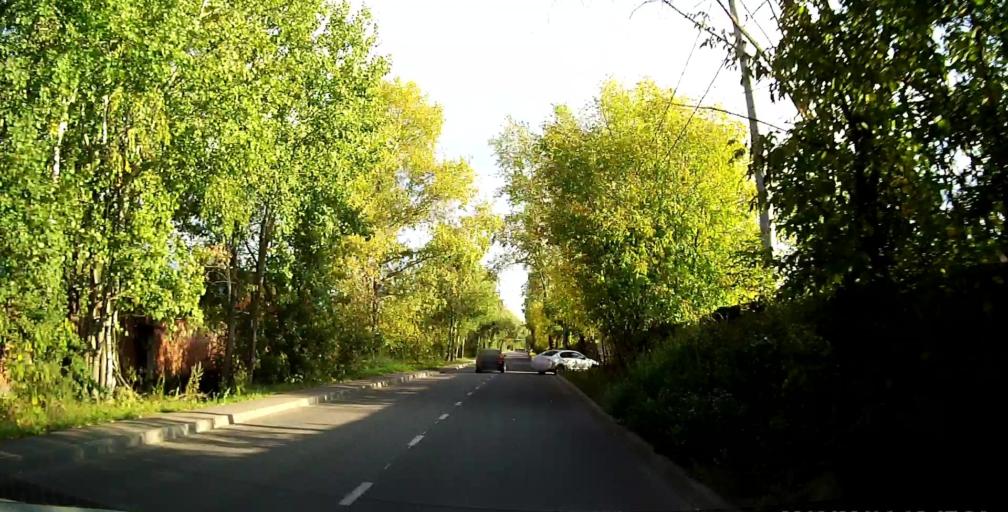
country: RU
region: Moskovskaya
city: Klimovsk
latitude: 55.3641
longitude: 37.5506
